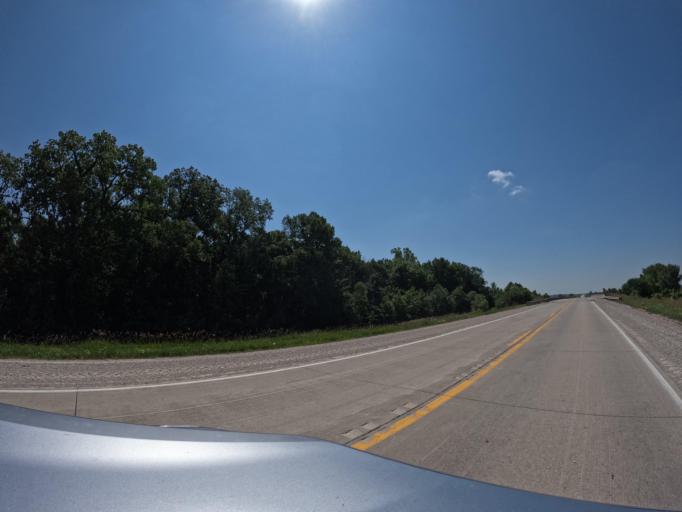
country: US
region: Iowa
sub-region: Keokuk County
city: Sigourney
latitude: 41.3023
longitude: -92.2048
